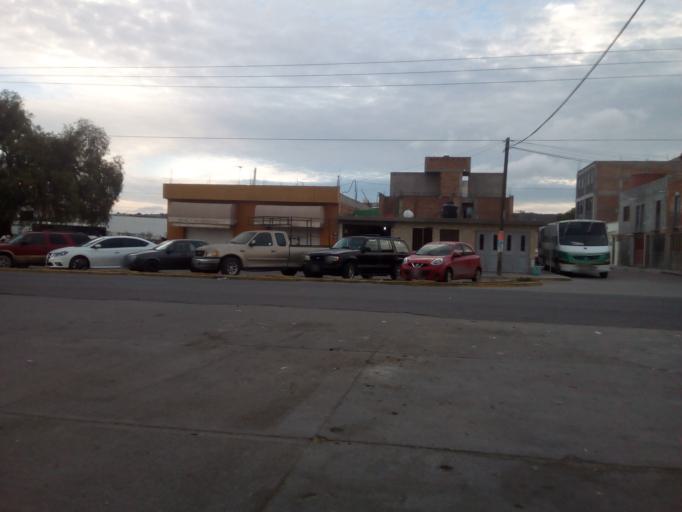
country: MX
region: Guanajuato
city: San Jose Iturbide
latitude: 21.0055
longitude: -100.3846
